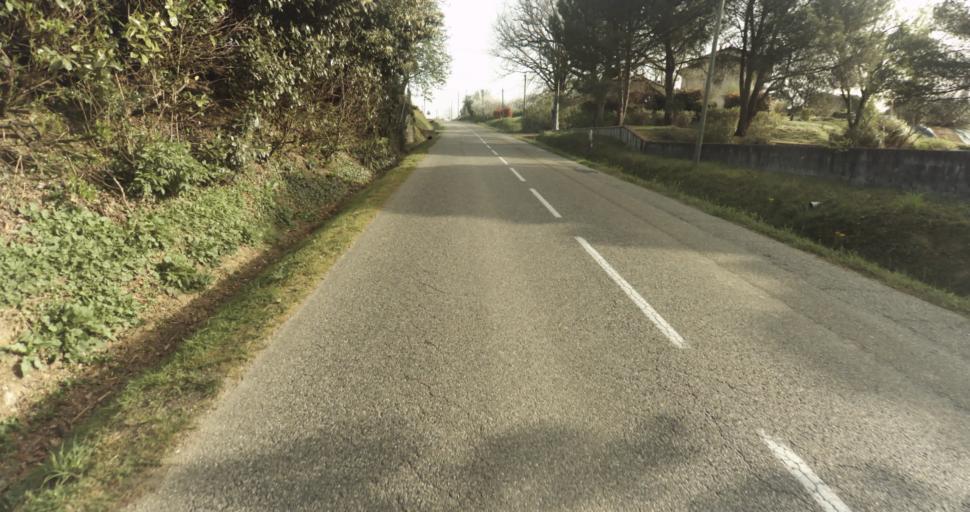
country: FR
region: Midi-Pyrenees
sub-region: Departement du Tarn-et-Garonne
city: Moissac
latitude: 44.1560
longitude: 1.0973
